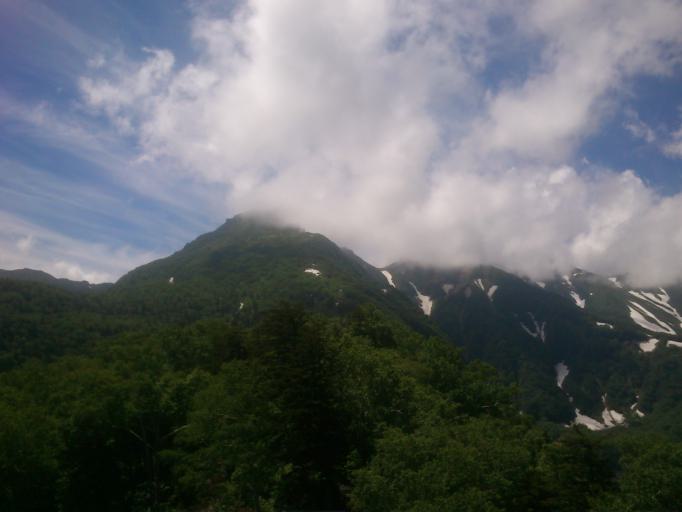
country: JP
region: Hokkaido
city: Kamikawa
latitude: 43.7269
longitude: 142.9445
